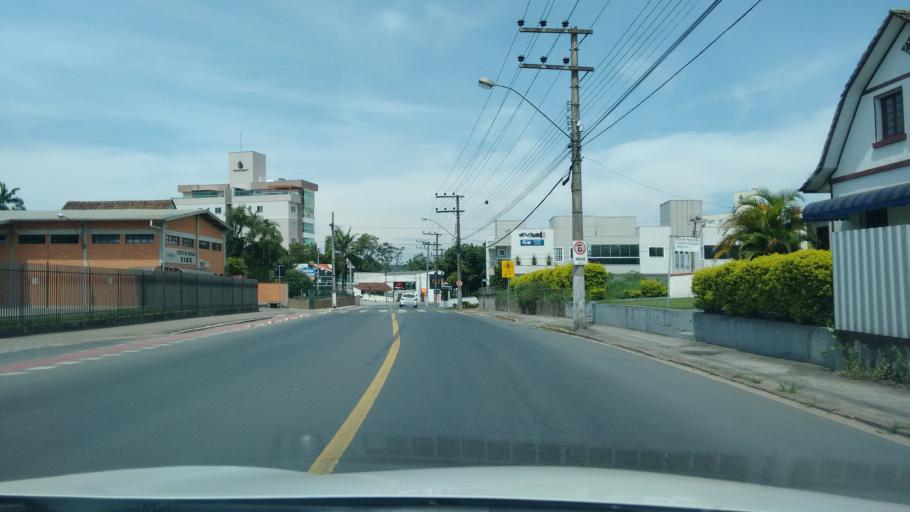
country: BR
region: Santa Catarina
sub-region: Timbo
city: Timbo
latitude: -26.8333
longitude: -49.2726
